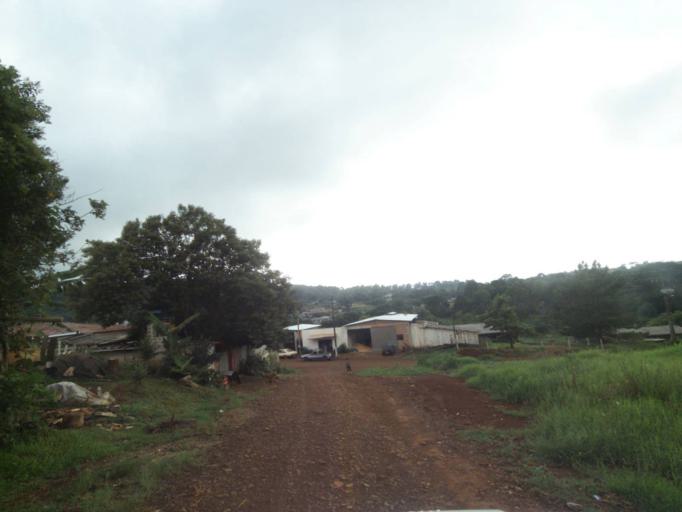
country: BR
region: Parana
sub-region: Pitanga
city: Pitanga
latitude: -24.9421
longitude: -51.8689
